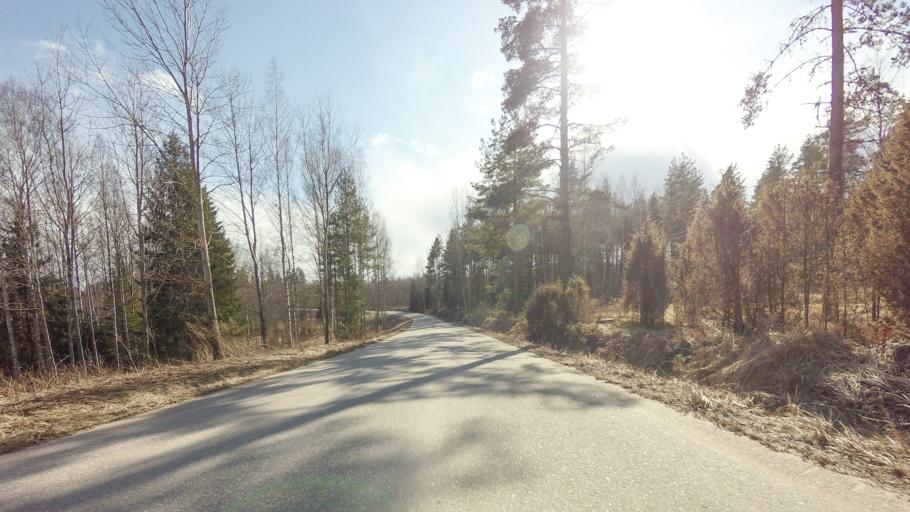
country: FI
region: Varsinais-Suomi
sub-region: Salo
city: Suomusjaervi
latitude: 60.3128
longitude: 23.6430
